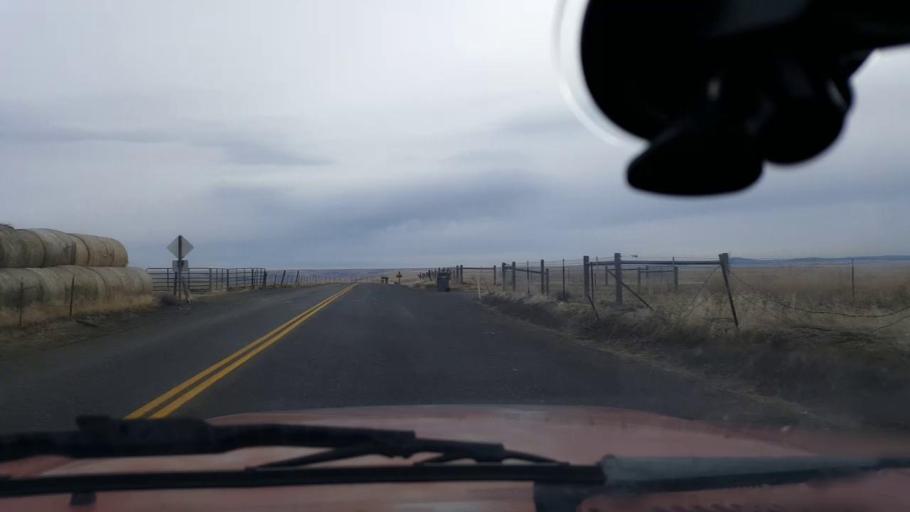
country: US
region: Washington
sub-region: Asotin County
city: Clarkston Heights-Vineland
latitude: 46.3786
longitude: -117.1450
